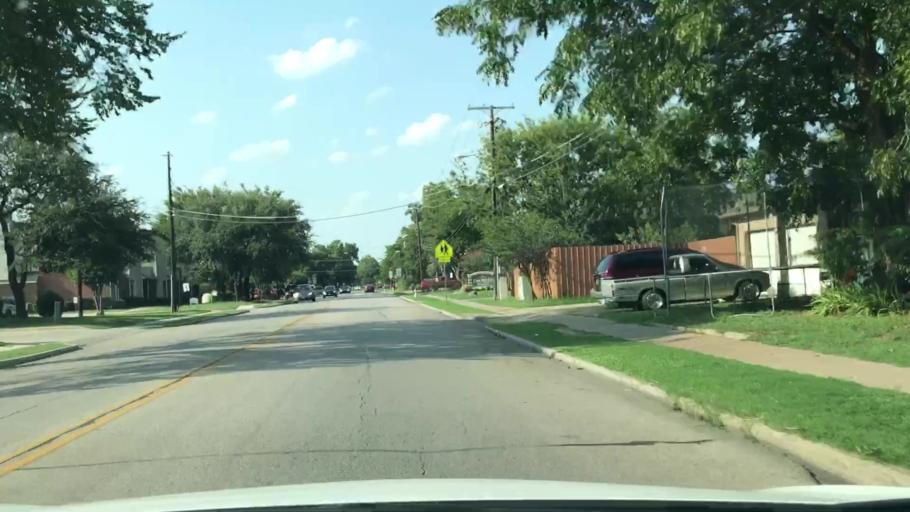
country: US
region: Texas
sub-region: Dallas County
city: Irving
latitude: 32.8202
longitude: -96.9342
